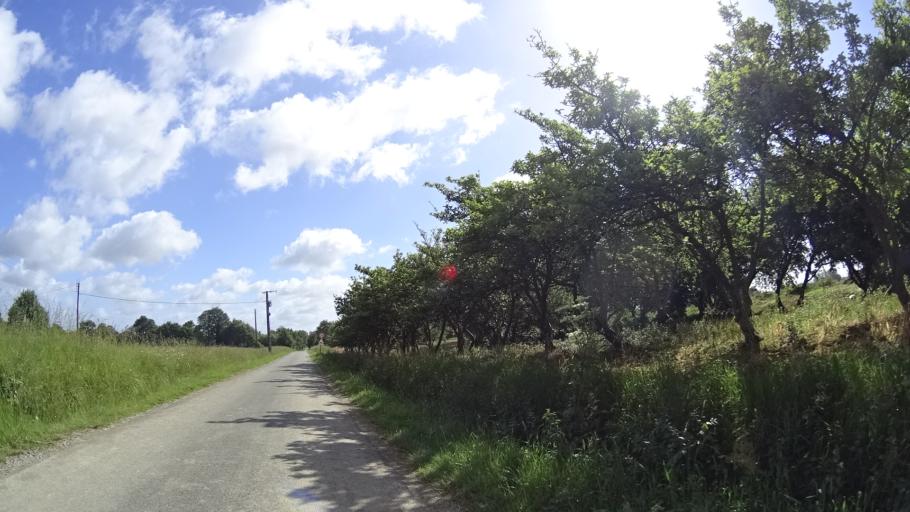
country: FR
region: Brittany
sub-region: Departement d'Ille-et-Vilaine
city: Melesse
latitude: 48.2045
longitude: -1.7204
